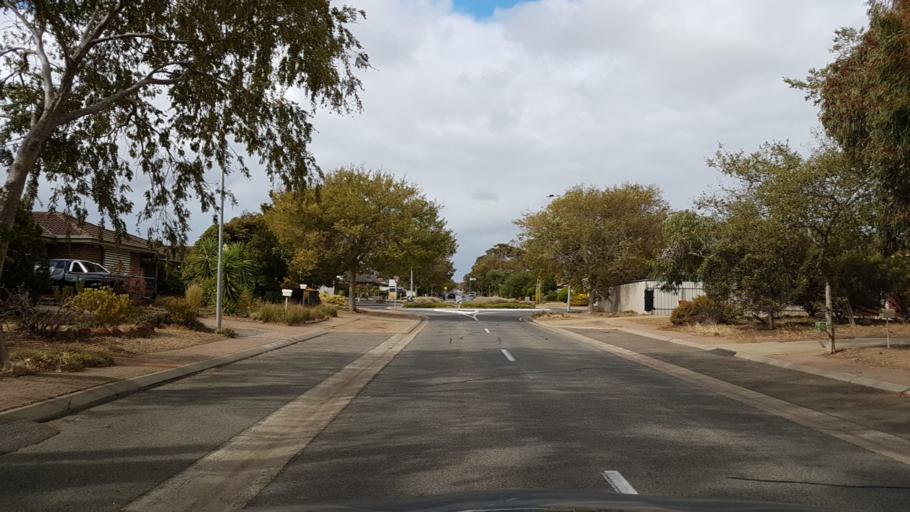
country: AU
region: South Australia
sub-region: Onkaparinga
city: Moana
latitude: -35.1979
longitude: 138.4814
